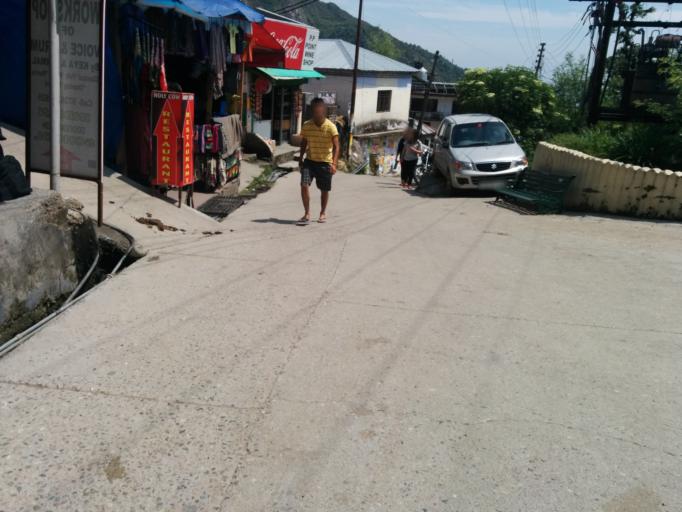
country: IN
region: Himachal Pradesh
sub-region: Kangra
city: Dharmsala
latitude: 32.2444
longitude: 76.3330
